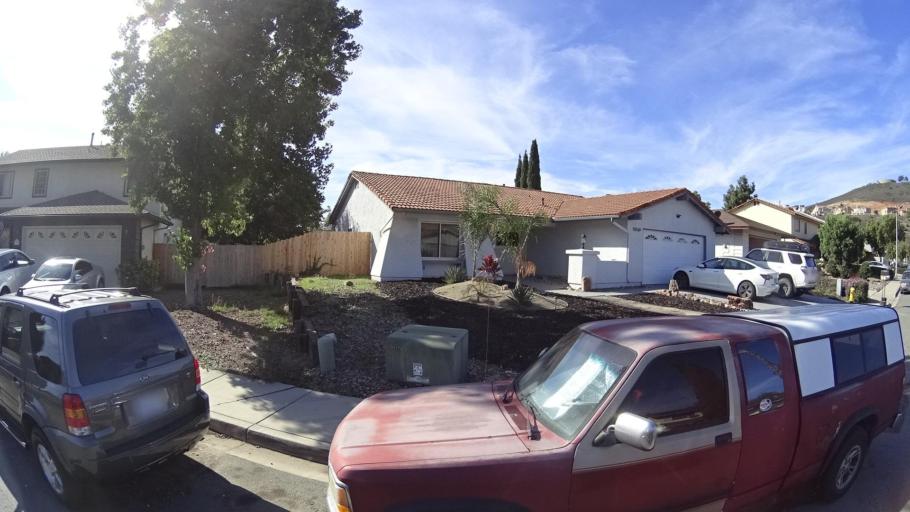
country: US
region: California
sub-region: San Diego County
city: La Presa
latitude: 32.7273
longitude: -116.9712
